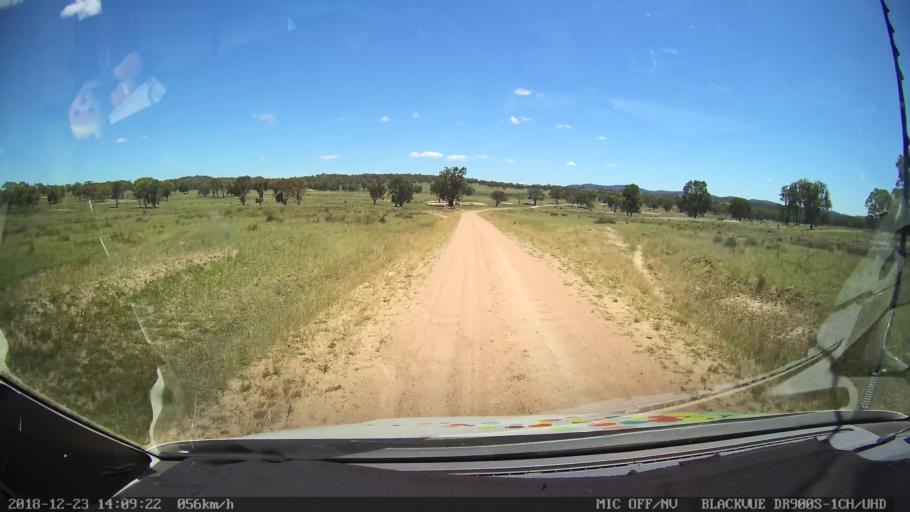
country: AU
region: New South Wales
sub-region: Tamworth Municipality
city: Manilla
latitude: -30.6448
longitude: 151.0626
